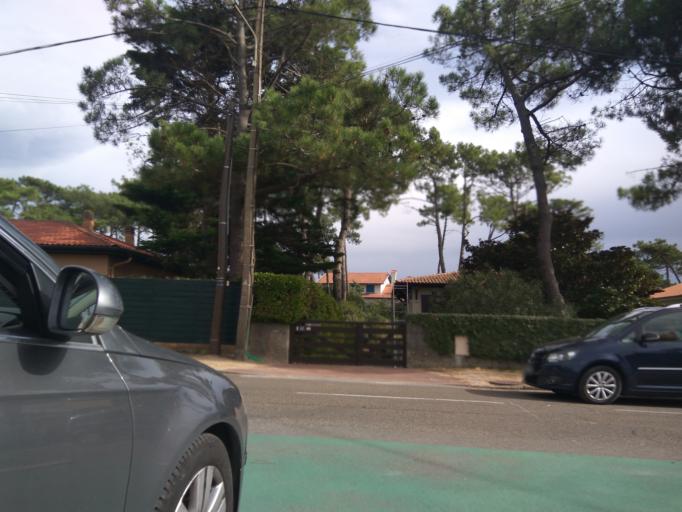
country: FR
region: Aquitaine
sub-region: Departement des Landes
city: Capbreton
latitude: 43.6462
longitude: -1.4403
